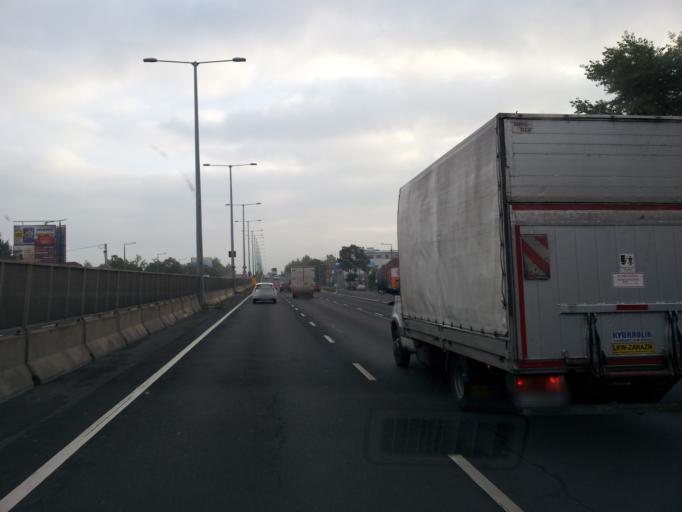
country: HU
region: Budapest
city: Budapest XV. keruelet
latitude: 47.5531
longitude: 19.1269
